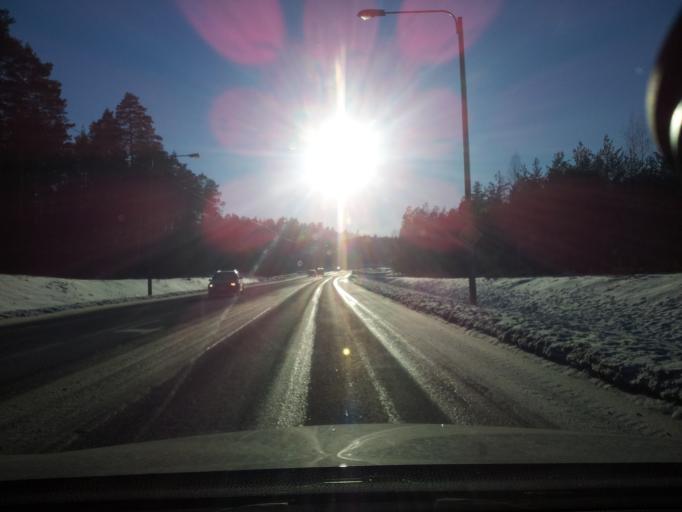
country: FI
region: Uusimaa
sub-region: Helsinki
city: Vihti
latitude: 60.3522
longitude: 24.3313
